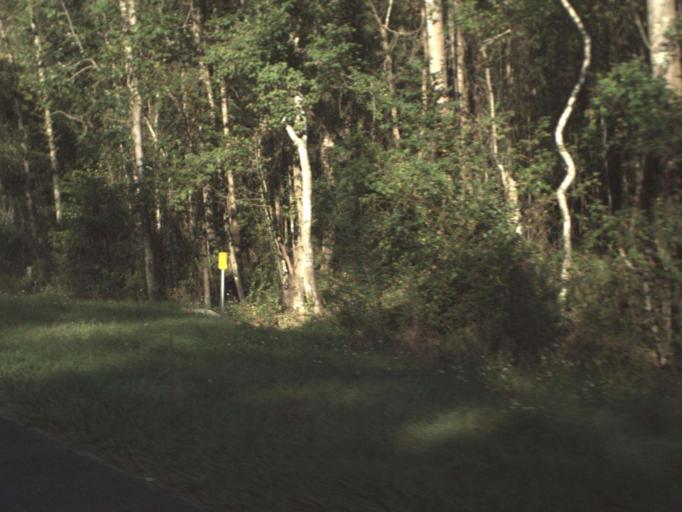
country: US
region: Florida
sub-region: Holmes County
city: Bonifay
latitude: 30.7200
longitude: -85.6158
